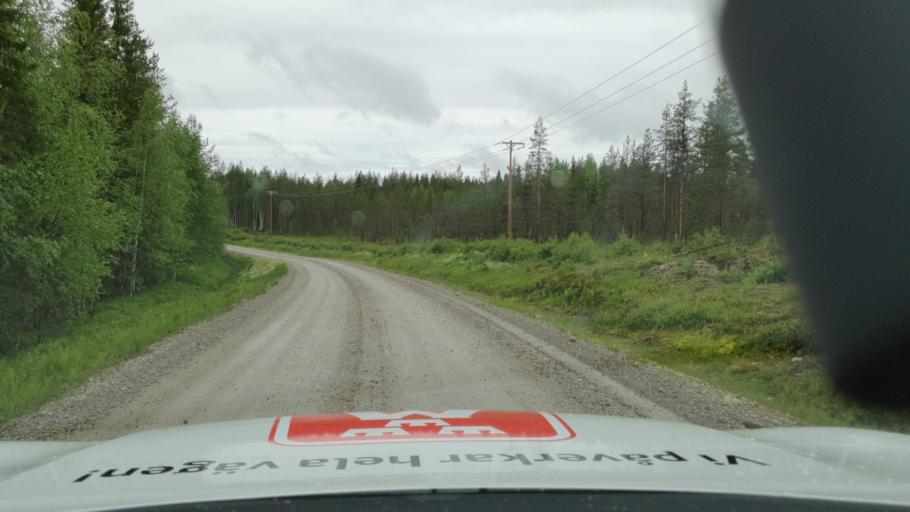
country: SE
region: Vaesterbotten
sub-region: Asele Kommun
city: Asele
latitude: 63.9744
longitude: 17.0429
